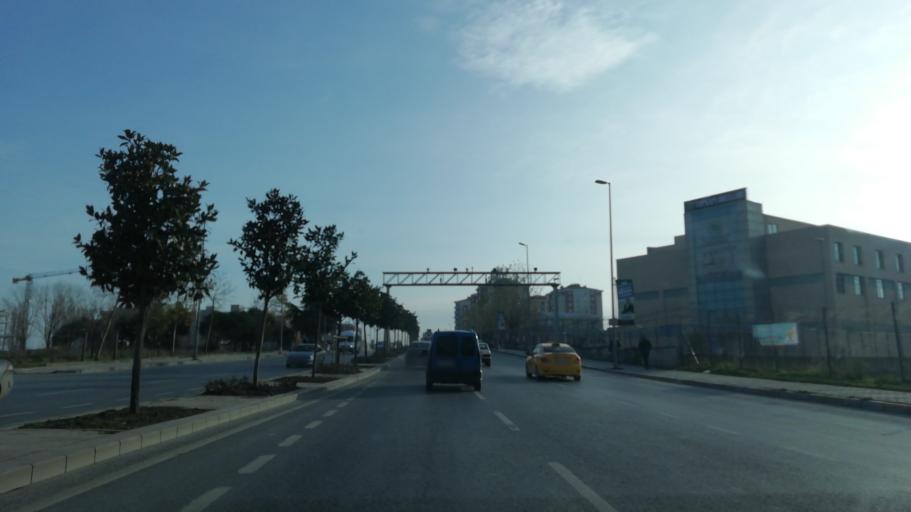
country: TR
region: Istanbul
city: Esenyurt
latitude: 41.0494
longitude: 28.6734
